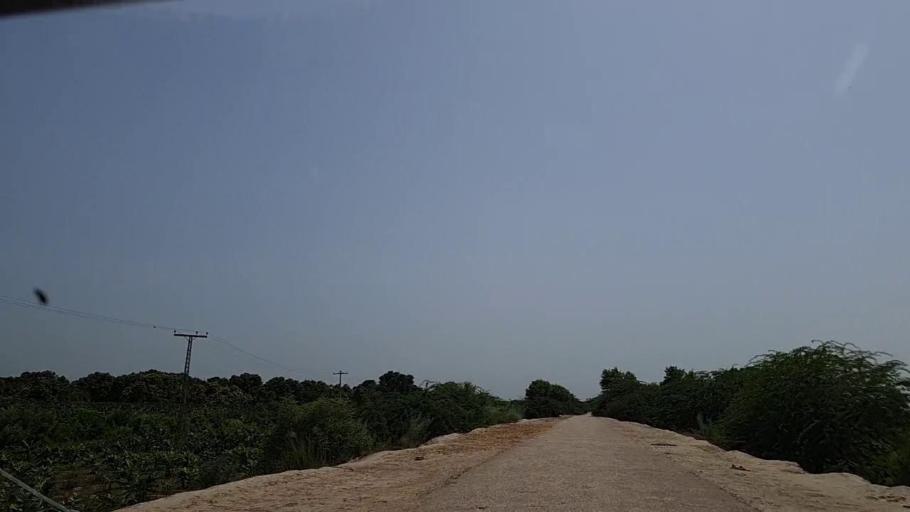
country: PK
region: Sindh
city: Kandiaro
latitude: 27.0433
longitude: 68.1304
